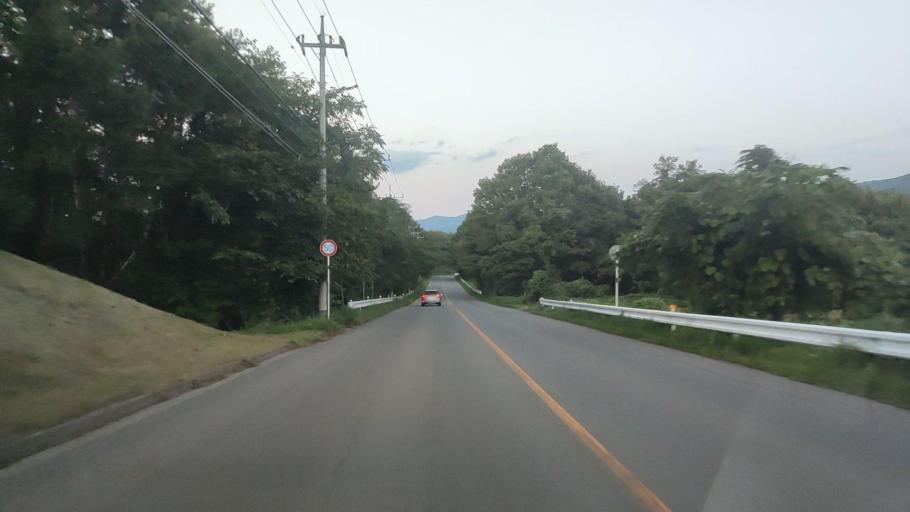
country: JP
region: Gunma
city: Nakanojomachi
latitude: 36.5292
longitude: 138.6047
